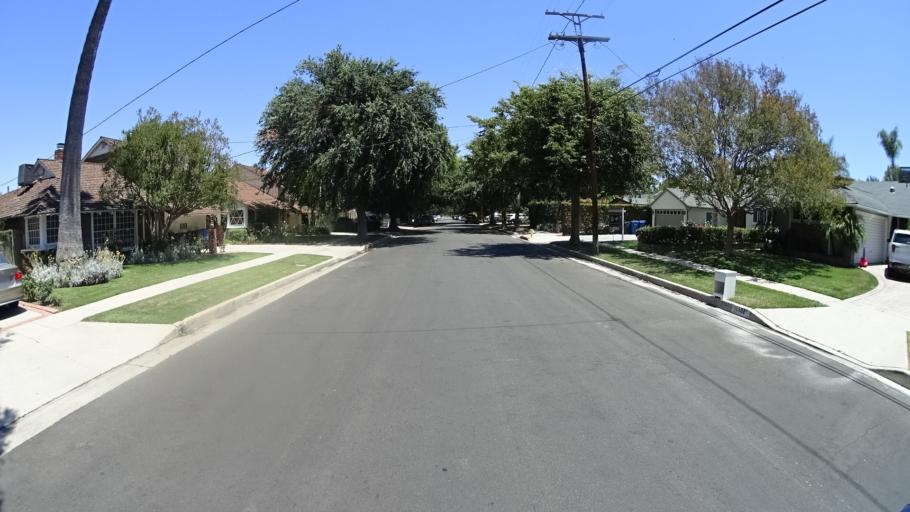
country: US
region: California
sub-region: Los Angeles County
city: Sherman Oaks
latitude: 34.1594
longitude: -118.4732
